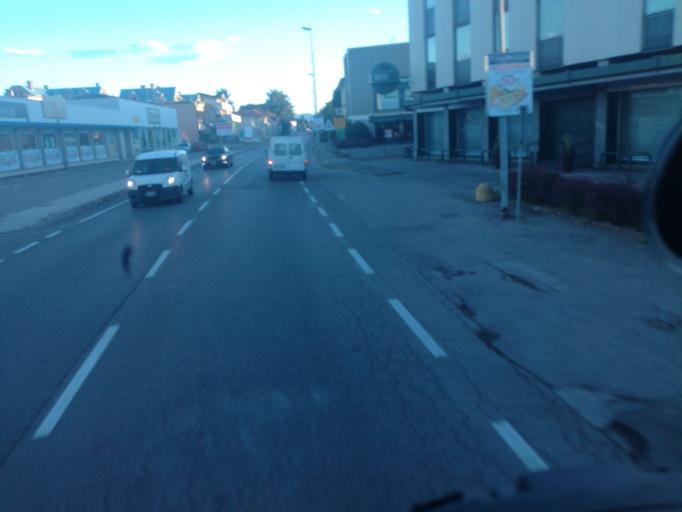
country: IT
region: Lombardy
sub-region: Provincia di Monza e Brianza
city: Limbiate
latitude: 45.6109
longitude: 9.1374
